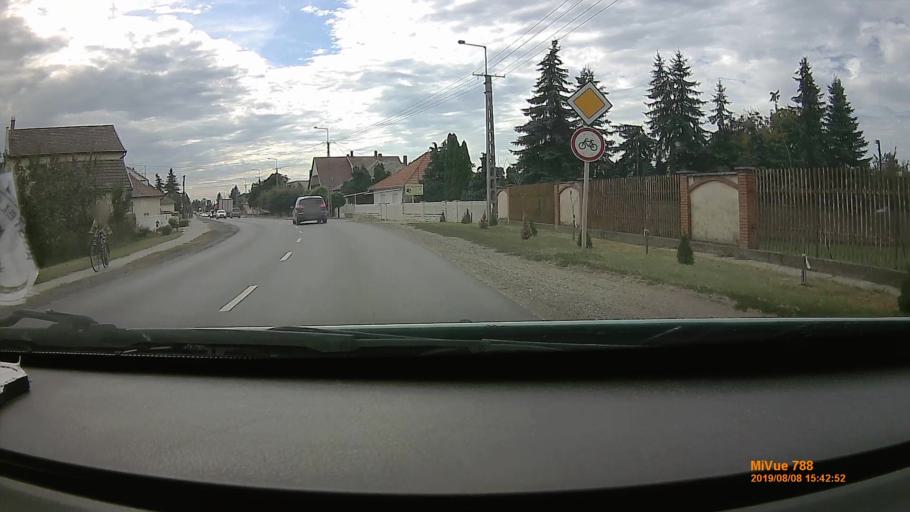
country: HU
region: Szabolcs-Szatmar-Bereg
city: Kocsord
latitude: 47.9395
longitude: 22.3950
